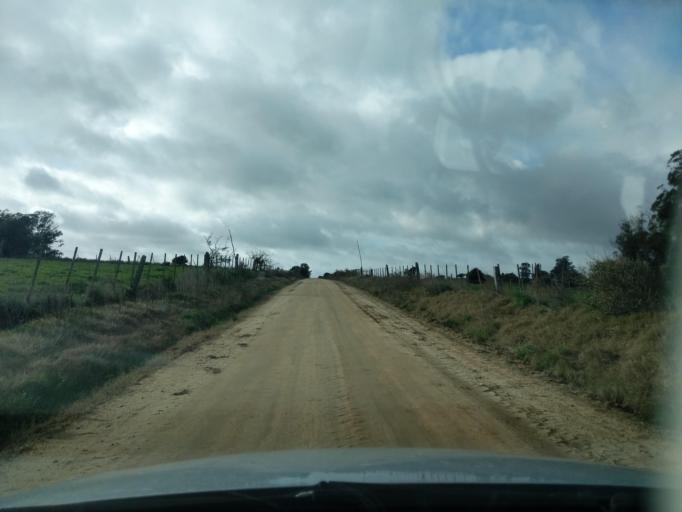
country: UY
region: Florida
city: Florida
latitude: -34.0603
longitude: -56.2096
